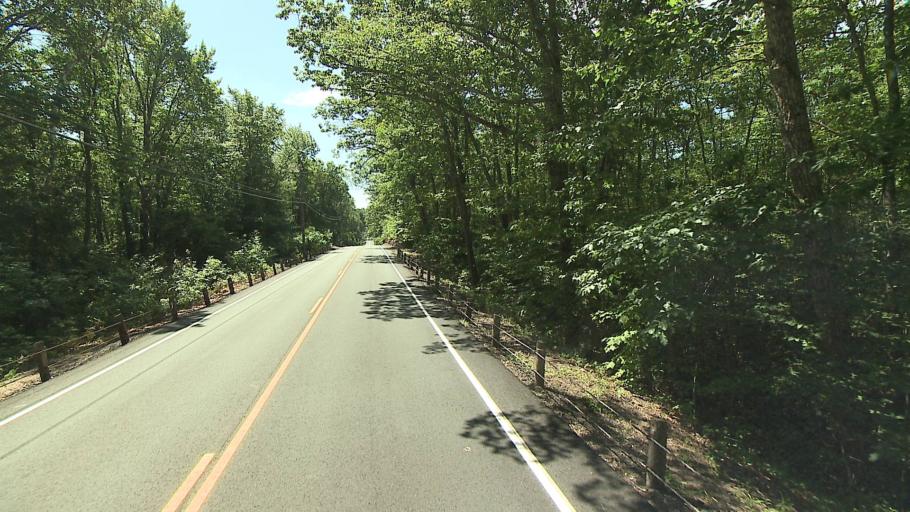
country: US
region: Connecticut
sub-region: Litchfield County
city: New Hartford Center
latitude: 41.9457
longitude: -72.9175
